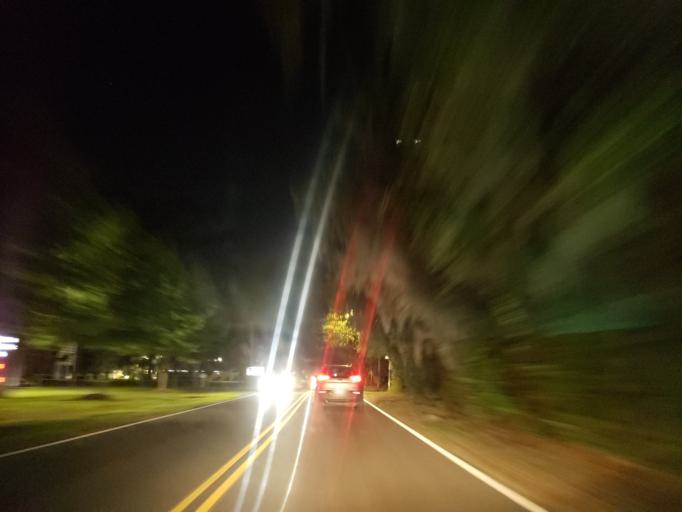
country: US
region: Georgia
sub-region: Chatham County
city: Isle of Hope
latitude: 32.0129
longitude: -81.0989
